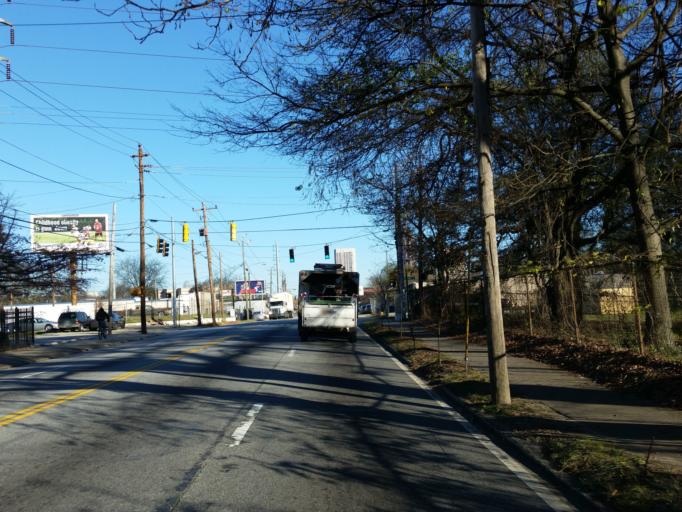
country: US
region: Georgia
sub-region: Fulton County
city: Atlanta
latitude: 33.7730
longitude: -84.4130
